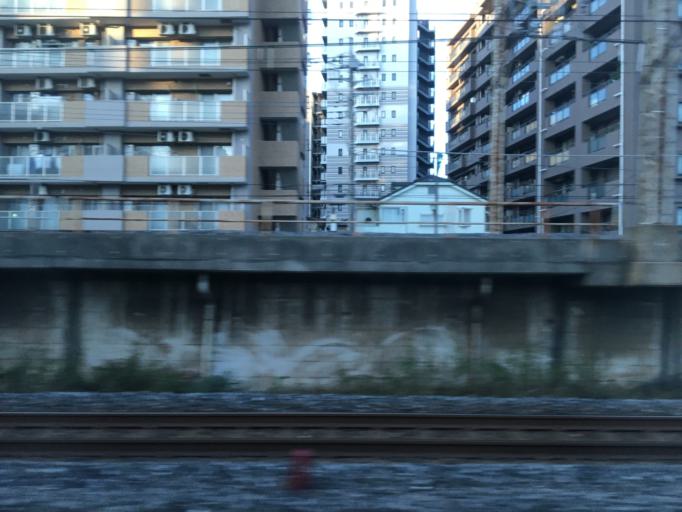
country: JP
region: Saitama
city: Yono
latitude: 35.8632
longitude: 139.6545
